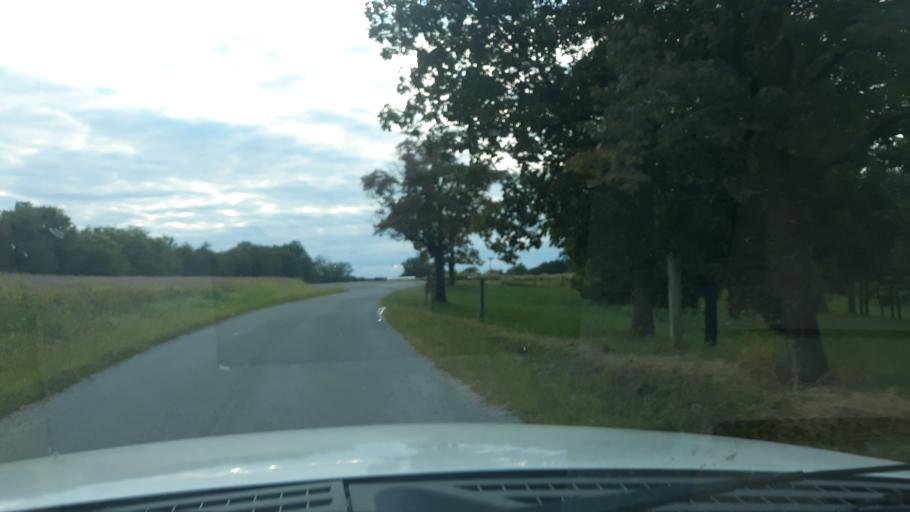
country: US
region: Illinois
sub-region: Saline County
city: Eldorado
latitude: 37.8363
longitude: -88.4837
